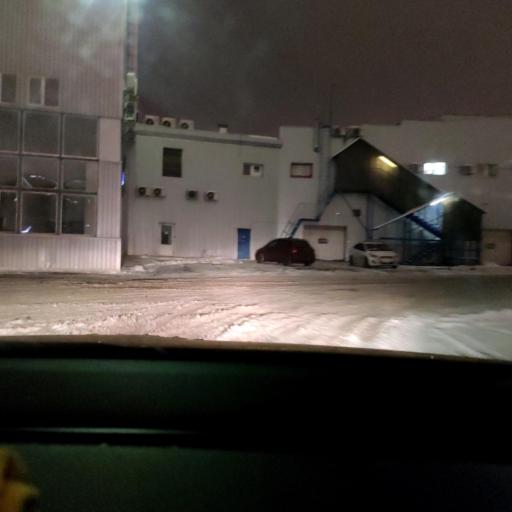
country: RU
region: Moscow
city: Rostokino
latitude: 55.8269
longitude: 37.6601
